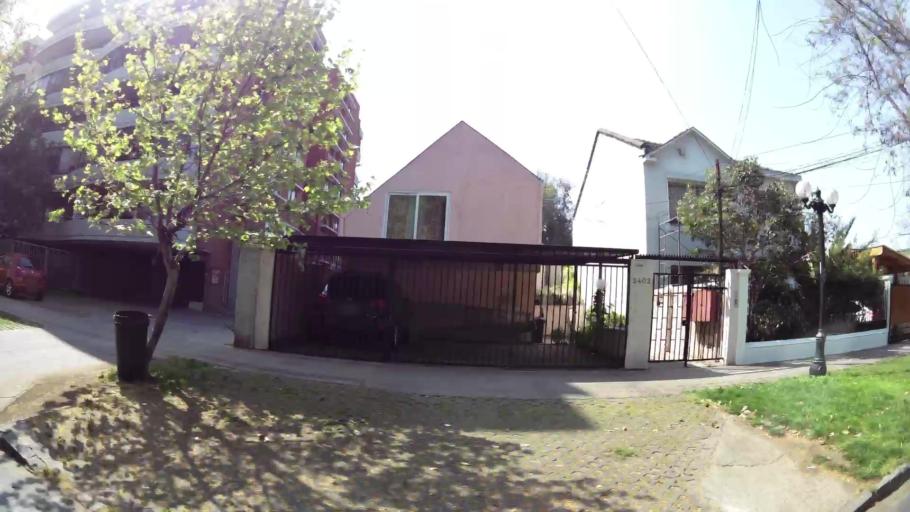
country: CL
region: Santiago Metropolitan
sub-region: Provincia de Santiago
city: Villa Presidente Frei, Nunoa, Santiago, Chile
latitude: -33.4420
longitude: -70.6015
